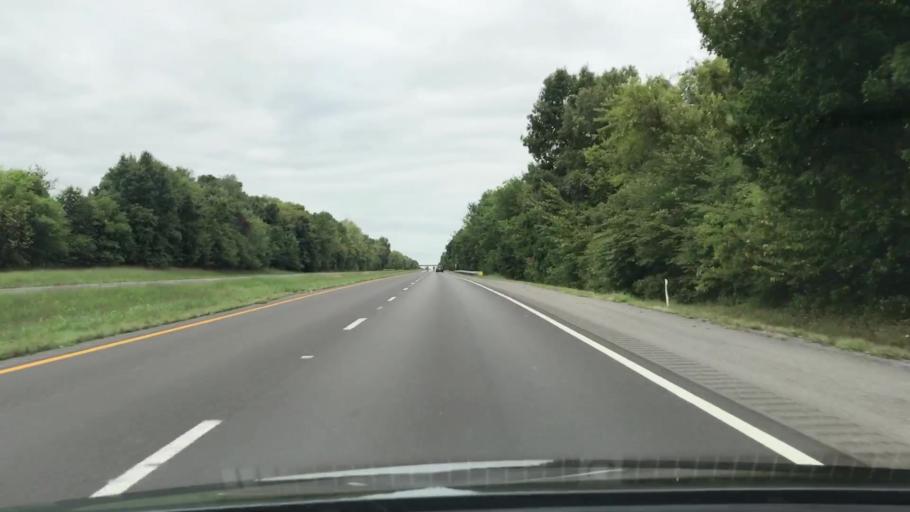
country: US
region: Kentucky
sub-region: Graves County
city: Mayfield
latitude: 36.6783
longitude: -88.7344
